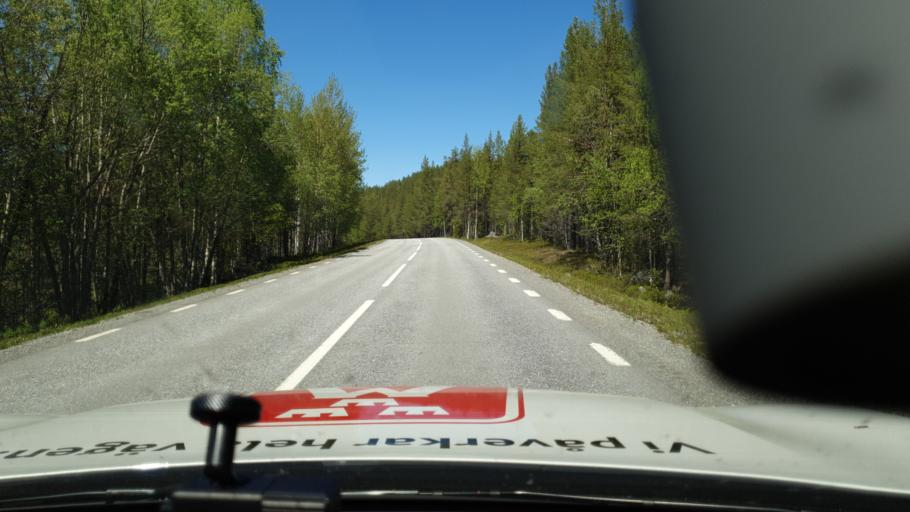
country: SE
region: Vaesterbotten
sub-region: Storumans Kommun
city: Storuman
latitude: 65.1558
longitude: 17.0618
